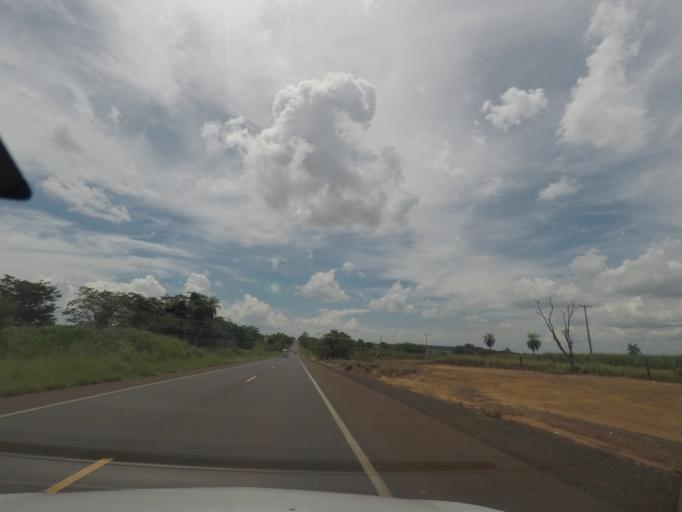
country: BR
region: Sao Paulo
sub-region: Barretos
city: Barretos
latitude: -20.3718
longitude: -48.6453
